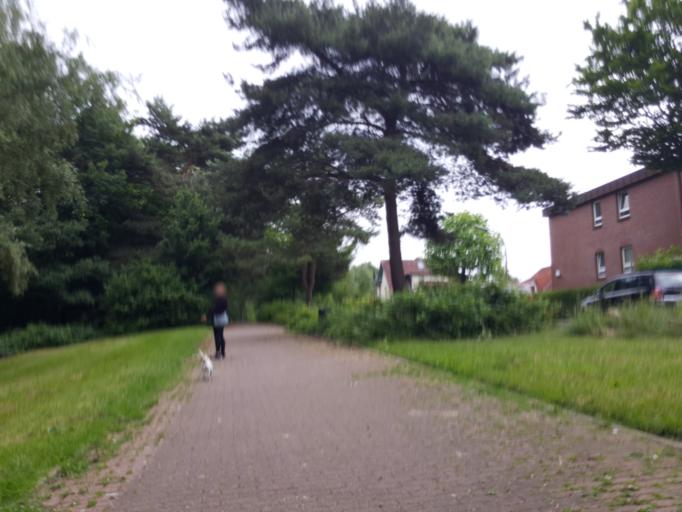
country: DE
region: Hamburg
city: Wandsbek
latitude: 53.5388
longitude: 10.1160
